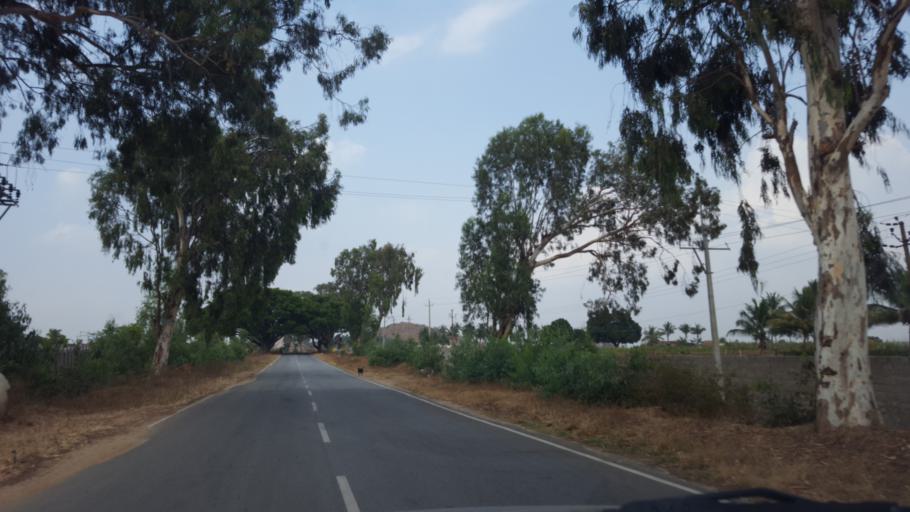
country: IN
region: Karnataka
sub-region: Chikkaballapur
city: Chik Ballapur
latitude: 13.3538
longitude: 77.6900
